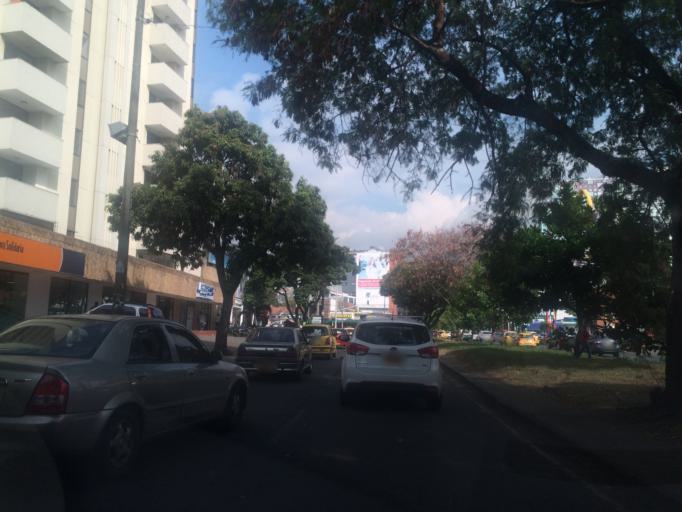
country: CO
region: Valle del Cauca
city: Cali
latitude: 3.4217
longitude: -76.5407
